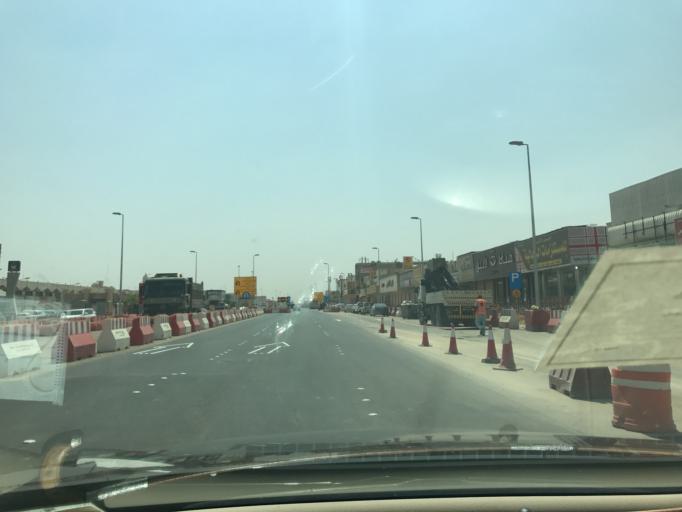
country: SA
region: Ar Riyad
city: Riyadh
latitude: 24.7498
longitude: 46.7724
